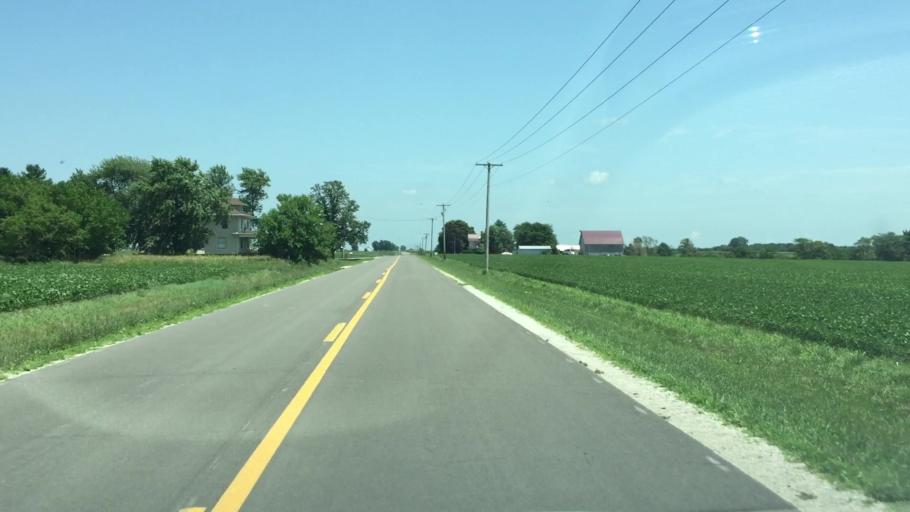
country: US
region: Illinois
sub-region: Hancock County
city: Carthage
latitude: 40.3279
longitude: -91.1734
